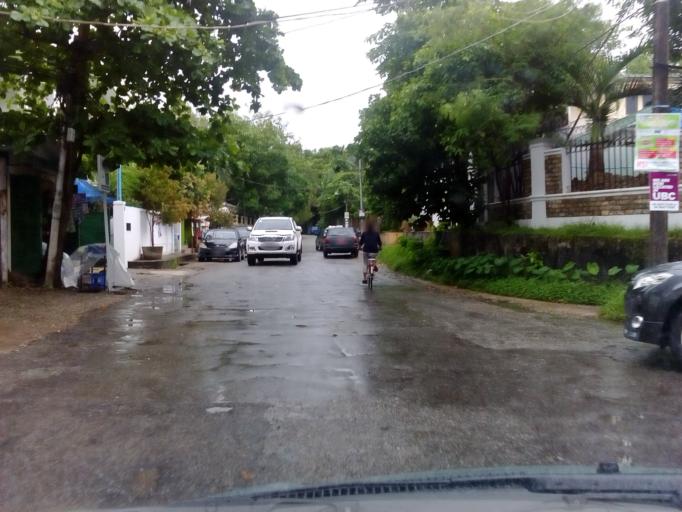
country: MM
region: Yangon
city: Yangon
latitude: 16.8171
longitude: 96.1498
